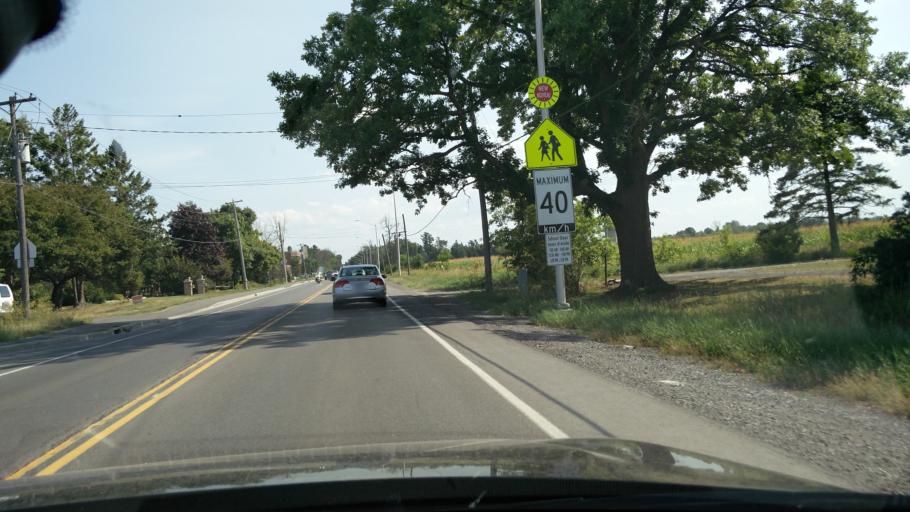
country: CA
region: Ontario
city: Bells Corners
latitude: 45.2656
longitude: -75.7435
